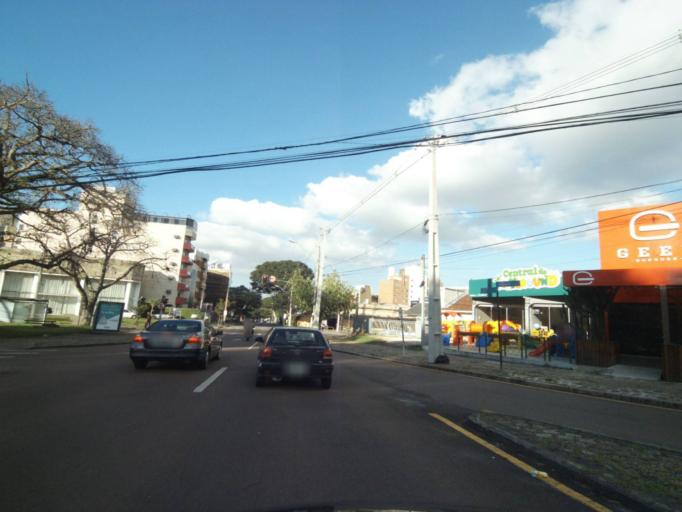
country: BR
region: Parana
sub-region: Curitiba
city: Curitiba
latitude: -25.4174
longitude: -49.2588
